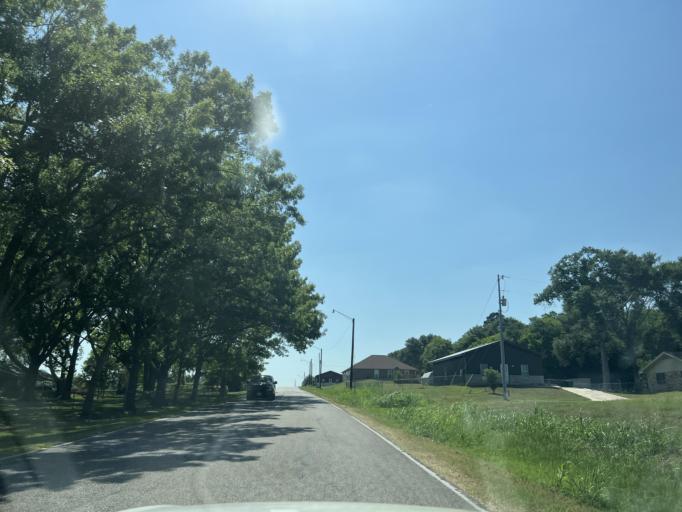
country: US
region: Texas
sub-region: Washington County
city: Brenham
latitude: 30.1622
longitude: -96.4196
